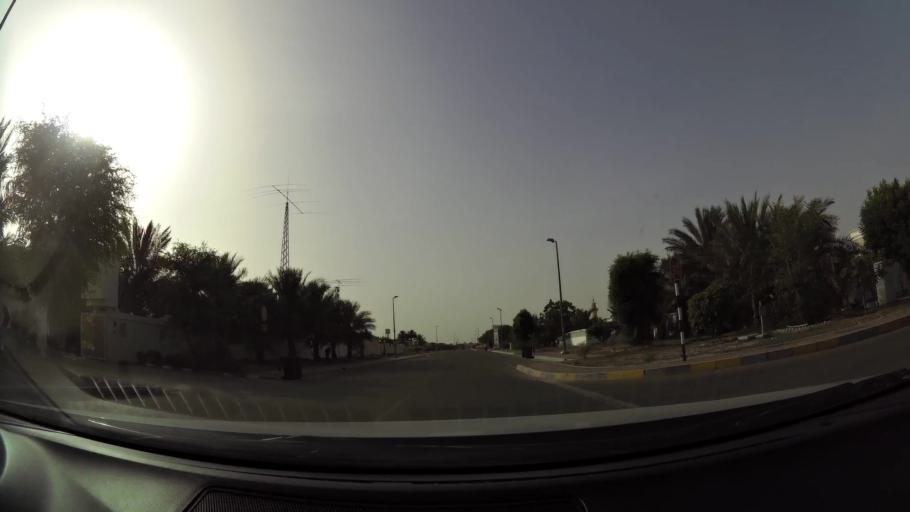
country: AE
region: Abu Dhabi
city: Al Ain
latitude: 24.2165
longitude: 55.6579
